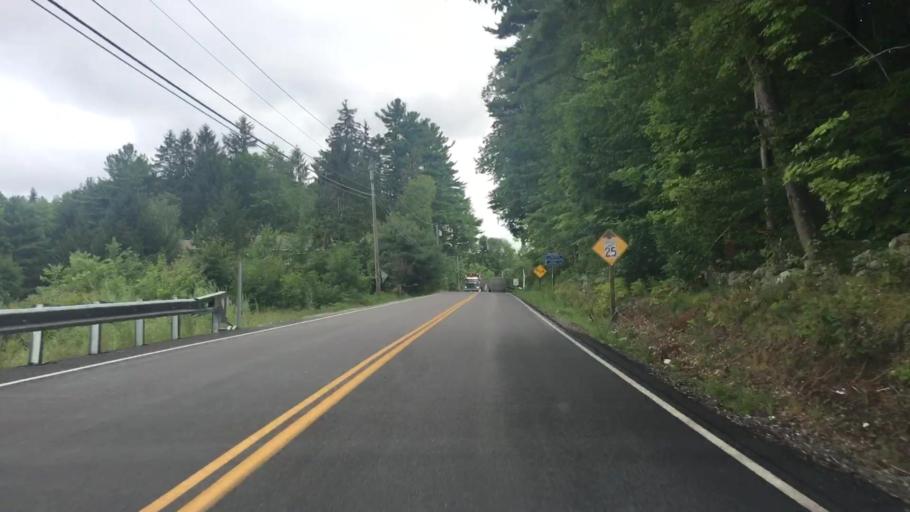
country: US
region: Maine
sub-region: York County
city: Limerick
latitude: 43.6926
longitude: -70.7971
